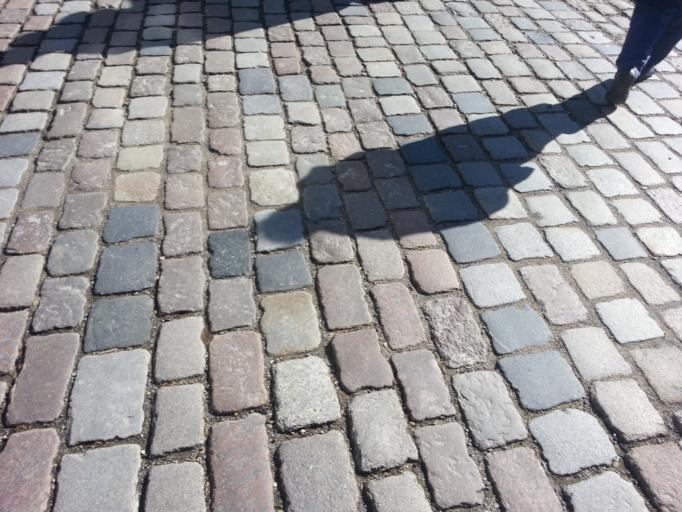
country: DE
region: Bavaria
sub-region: Swabia
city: Lindau
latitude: 47.5452
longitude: 9.6844
